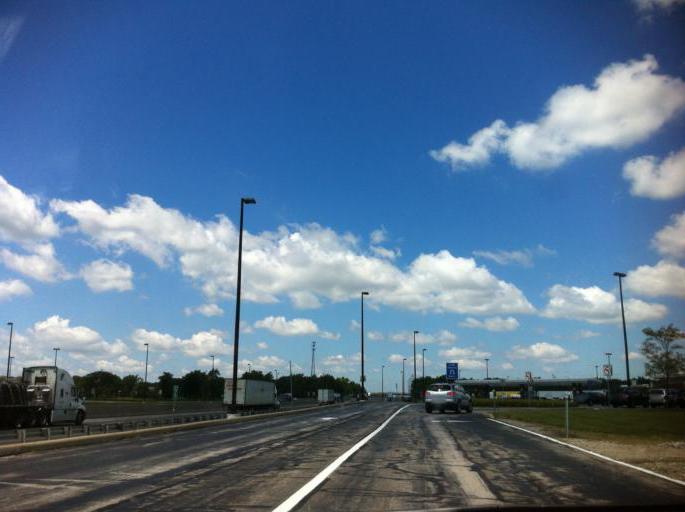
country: US
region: Ohio
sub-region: Ottawa County
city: Genoa
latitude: 41.4900
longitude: -83.3671
